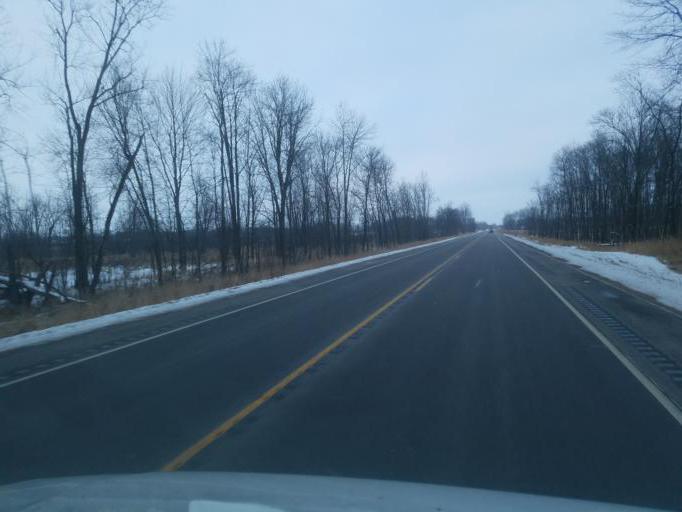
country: US
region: Wisconsin
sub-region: Waupaca County
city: New London
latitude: 44.4017
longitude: -88.7546
